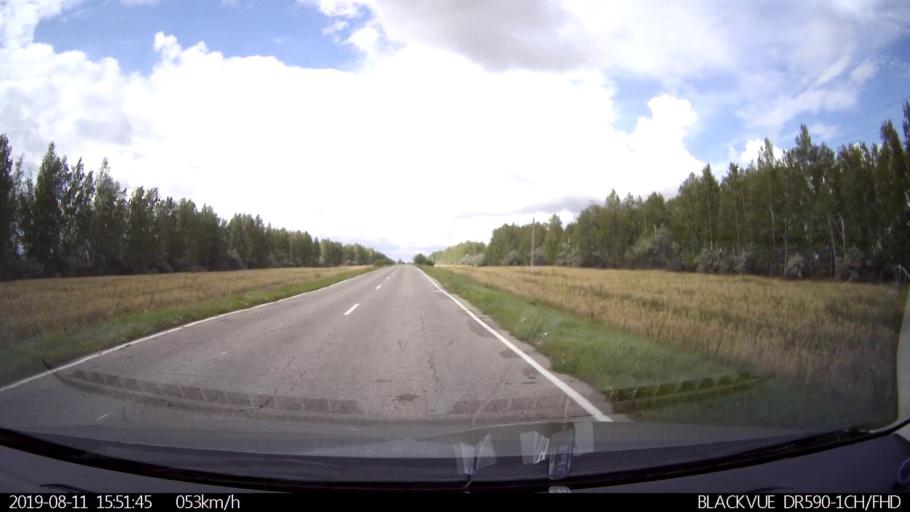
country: RU
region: Ulyanovsk
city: Ignatovka
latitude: 53.9212
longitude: 47.6562
